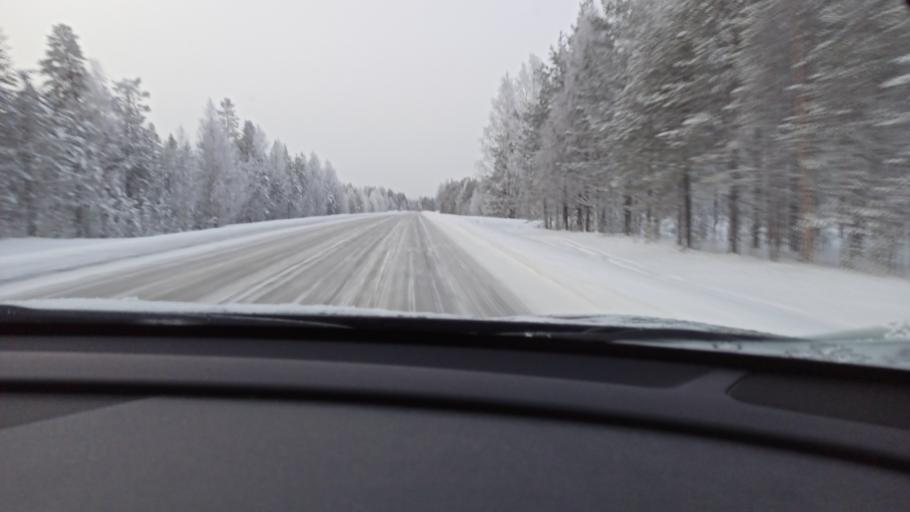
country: FI
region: Lapland
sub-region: Pohjois-Lappi
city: Sodankylae
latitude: 66.9334
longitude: 26.2651
